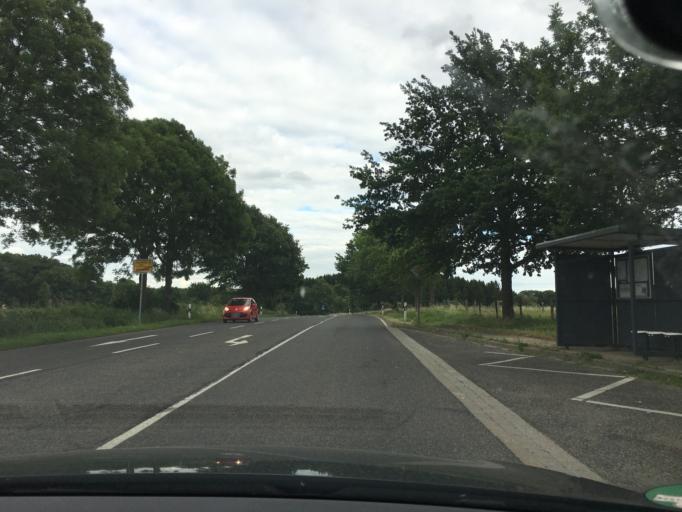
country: DE
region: North Rhine-Westphalia
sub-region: Regierungsbezirk Koln
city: Langerwehe
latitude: 50.7716
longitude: 6.3106
